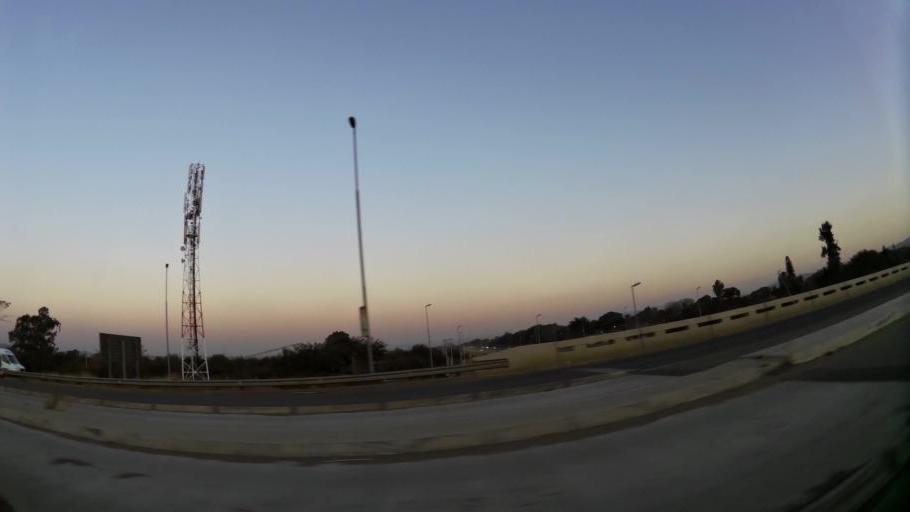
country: ZA
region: North-West
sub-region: Bojanala Platinum District Municipality
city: Rustenburg
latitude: -25.6469
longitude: 27.2561
